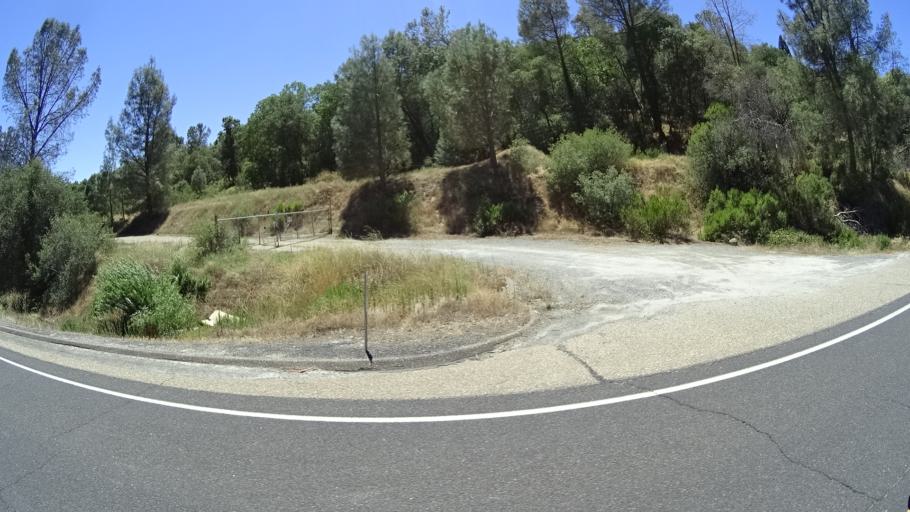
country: US
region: California
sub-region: Calaveras County
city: San Andreas
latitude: 38.1707
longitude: -120.6734
